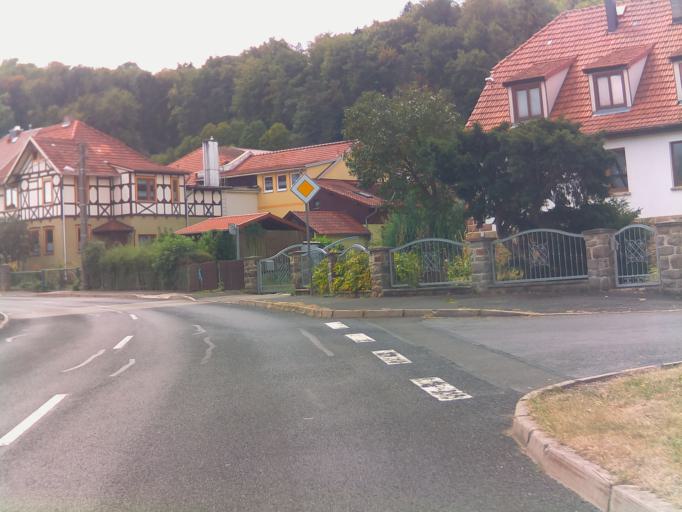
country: DE
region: Thuringia
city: Wolfershausen
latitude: 50.4674
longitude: 10.4384
